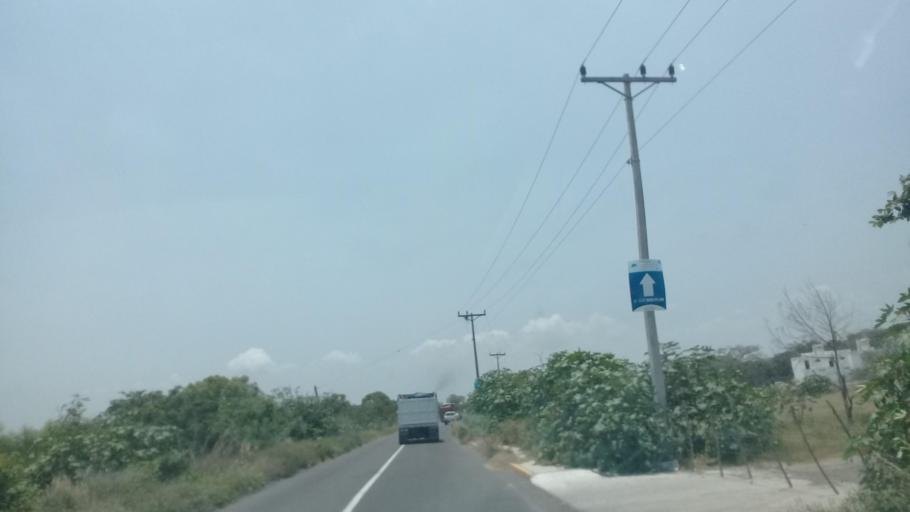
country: MX
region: Veracruz
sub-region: Veracruz
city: Hacienda Sotavento
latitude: 19.1445
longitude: -96.1722
